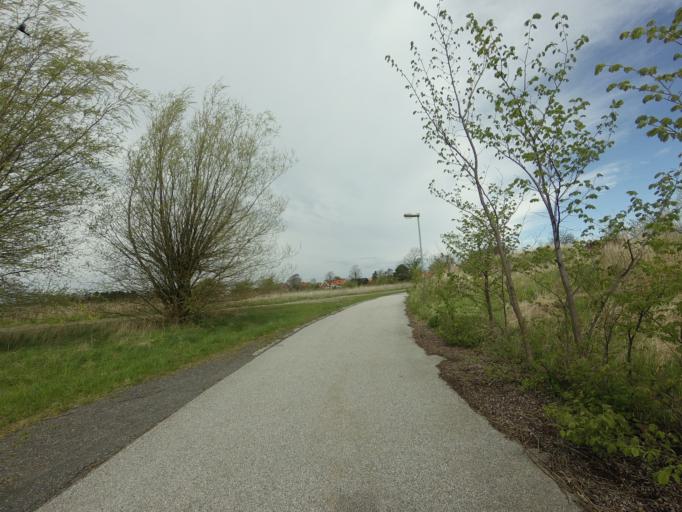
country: SE
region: Skane
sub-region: Malmo
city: Bunkeflostrand
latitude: 55.5500
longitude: 12.9665
